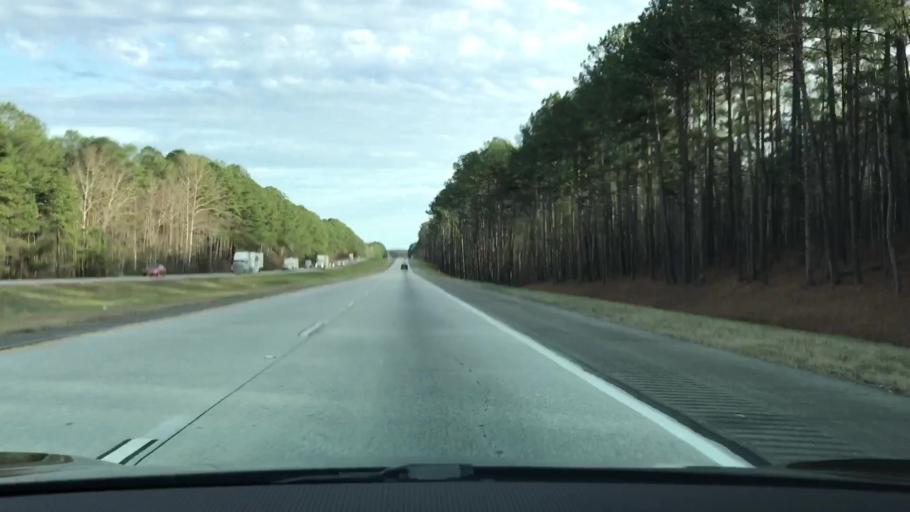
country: US
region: Georgia
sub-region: Taliaferro County
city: Crawfordville
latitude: 33.5088
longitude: -82.8407
